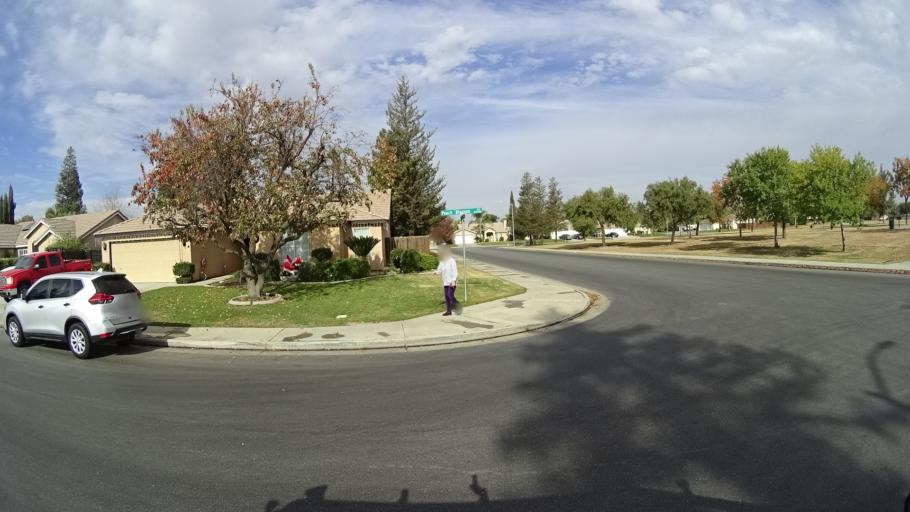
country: US
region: California
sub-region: Kern County
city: Greenacres
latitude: 35.4101
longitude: -119.1215
